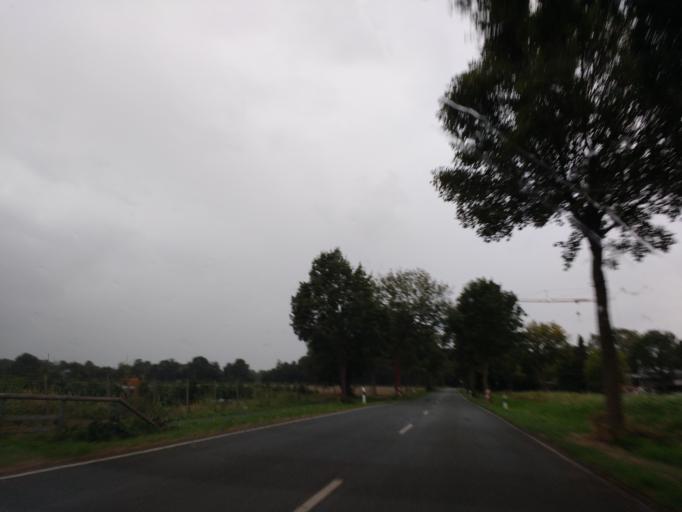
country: DE
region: North Rhine-Westphalia
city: Rietberg
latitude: 51.7414
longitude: 8.4463
